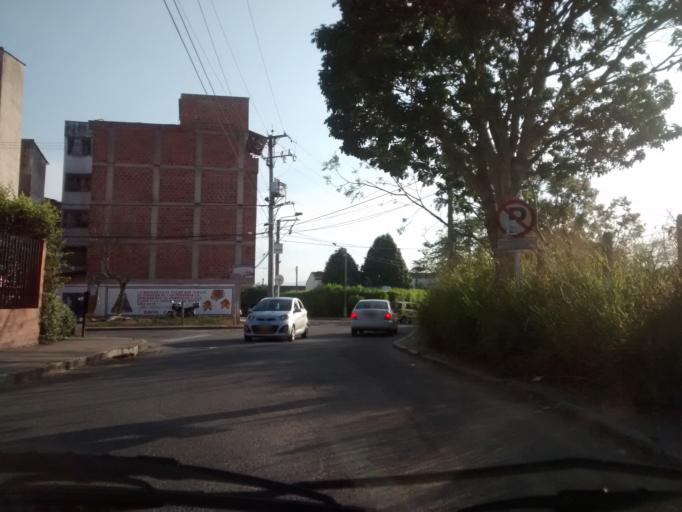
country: CO
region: Santander
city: Bucaramanga
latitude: 7.0967
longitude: -73.1340
